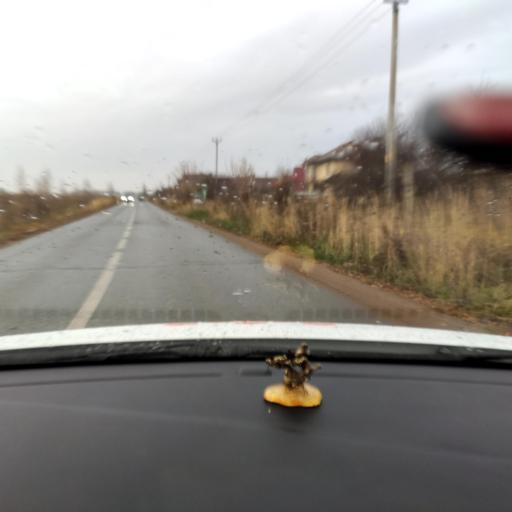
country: RU
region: Tatarstan
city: Vysokaya Gora
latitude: 55.8305
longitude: 49.2277
